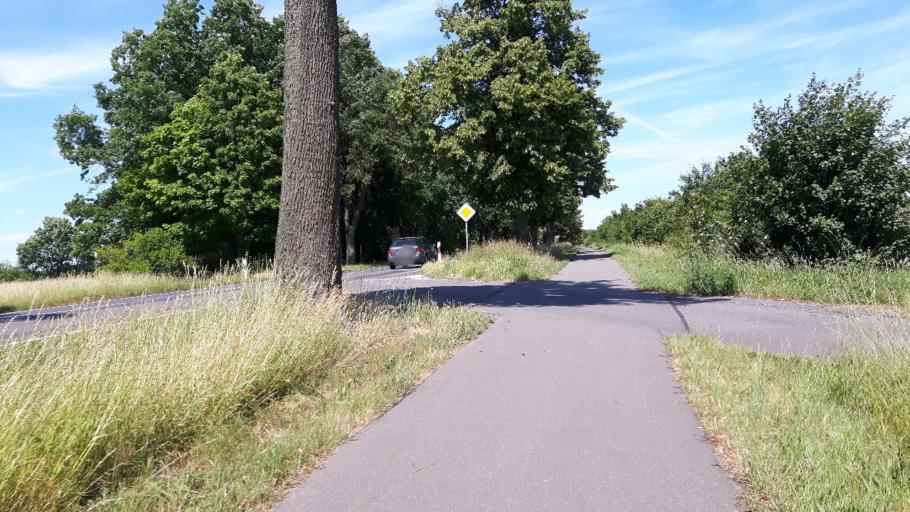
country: DE
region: Brandenburg
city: Treuenbrietzen
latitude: 52.0414
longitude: 12.8103
